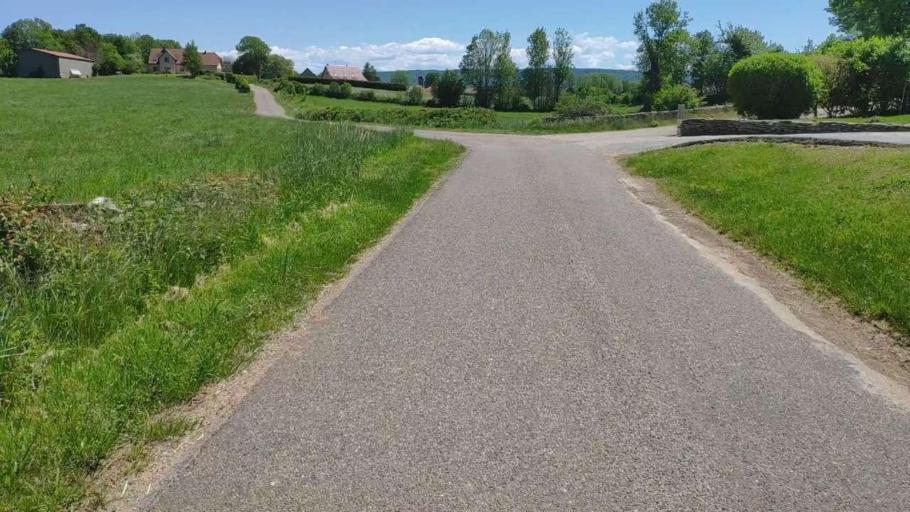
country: FR
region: Franche-Comte
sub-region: Departement du Jura
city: Poligny
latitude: 46.7362
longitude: 5.6902
